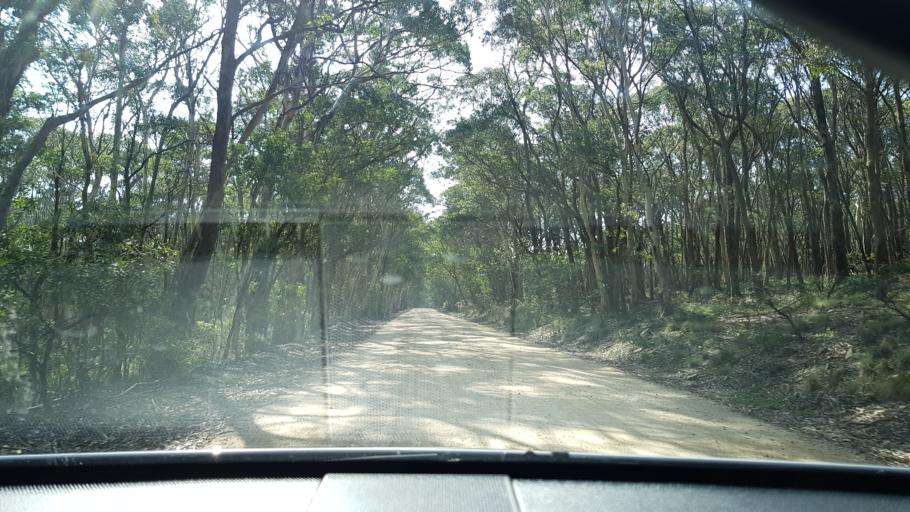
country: AU
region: New South Wales
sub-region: Oberon
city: Oberon
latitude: -33.9858
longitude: 150.0619
